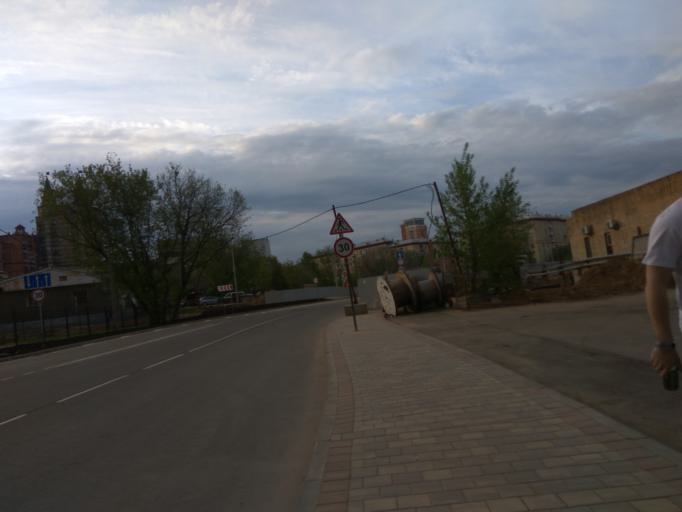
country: RU
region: Moscow
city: Sokol
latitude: 55.7877
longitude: 37.5000
